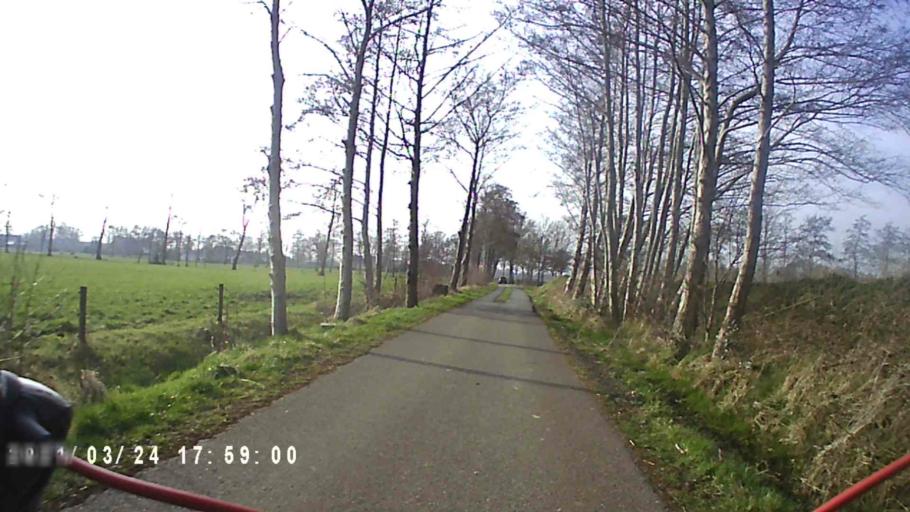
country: NL
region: Groningen
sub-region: Gemeente Leek
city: Leek
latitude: 53.1308
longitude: 6.3598
